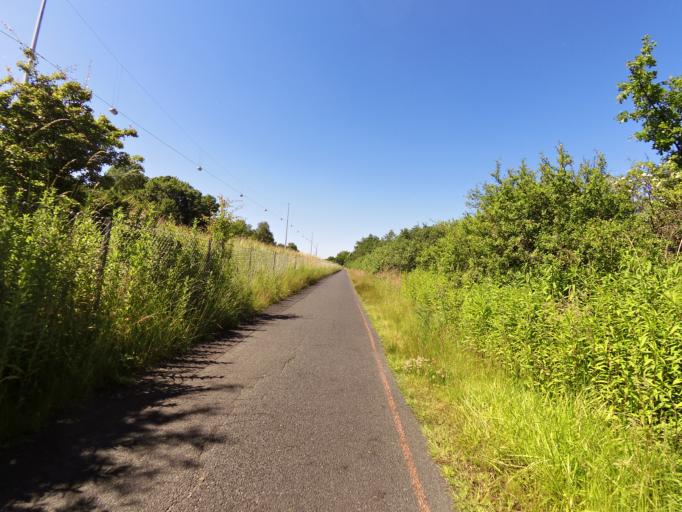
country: DK
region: Capital Region
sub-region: Gladsaxe Municipality
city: Buddinge
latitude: 55.7225
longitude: 12.4918
